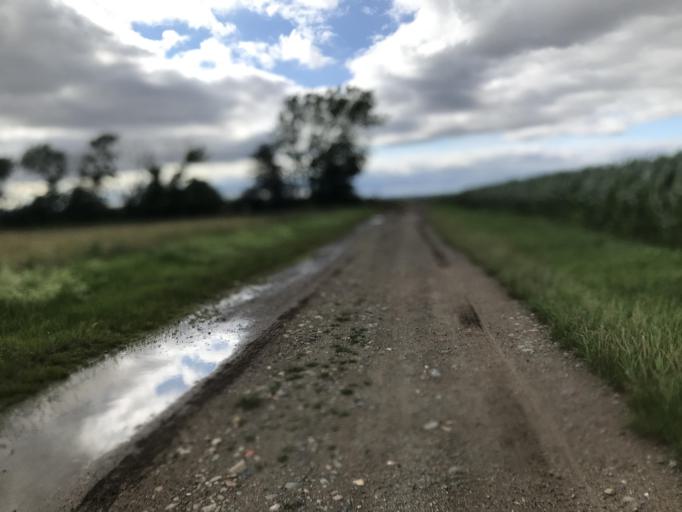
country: DE
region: Saxony-Anhalt
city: Ditfurt
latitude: 51.8170
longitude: 11.2266
